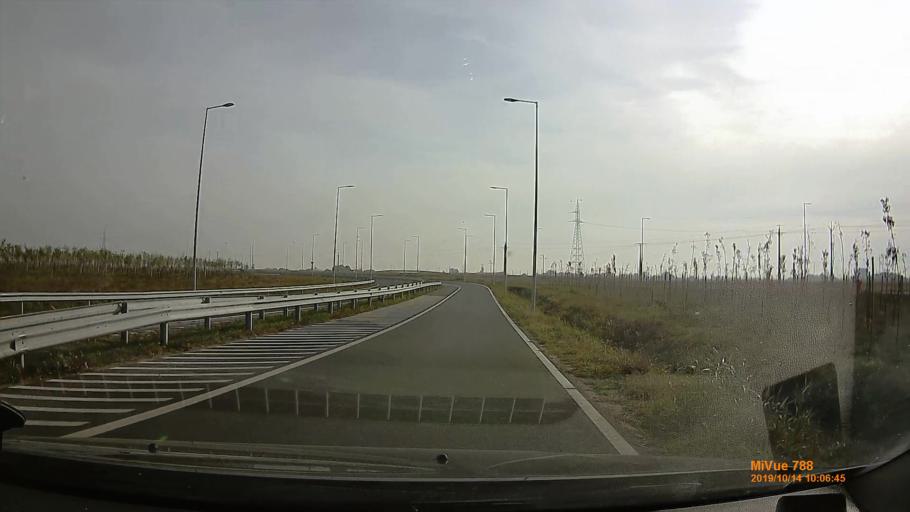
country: HU
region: Pest
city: Cegled
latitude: 47.1942
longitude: 19.8128
